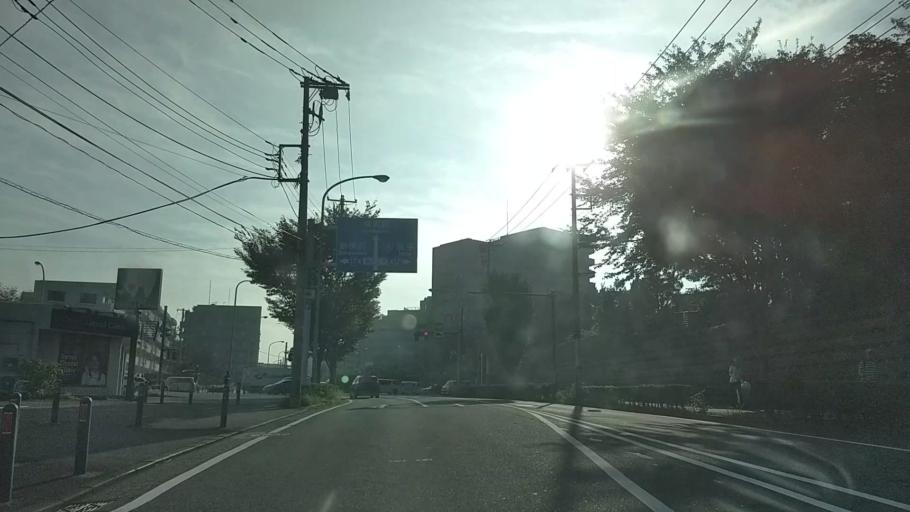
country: JP
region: Kanagawa
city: Yokohama
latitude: 35.4357
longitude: 139.5619
